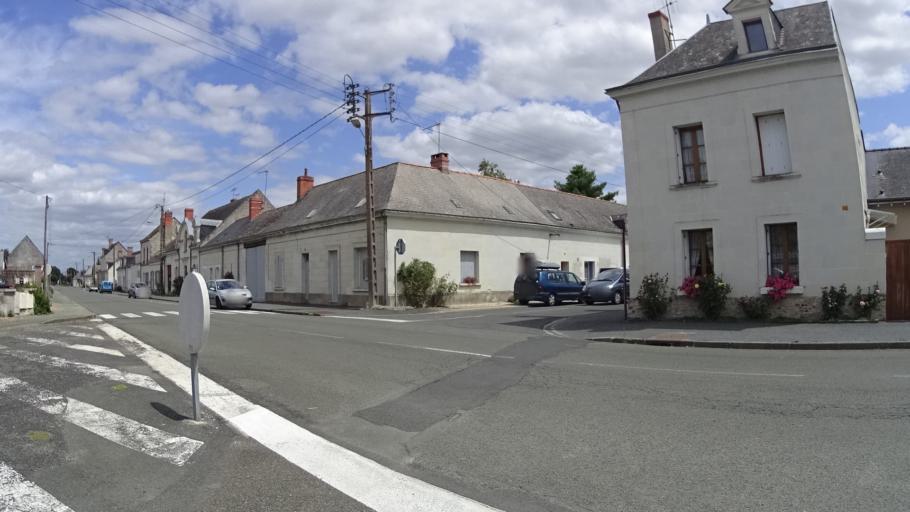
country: FR
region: Pays de la Loire
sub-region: Departement de Maine-et-Loire
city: La Menitre
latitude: 47.4030
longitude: -0.2681
